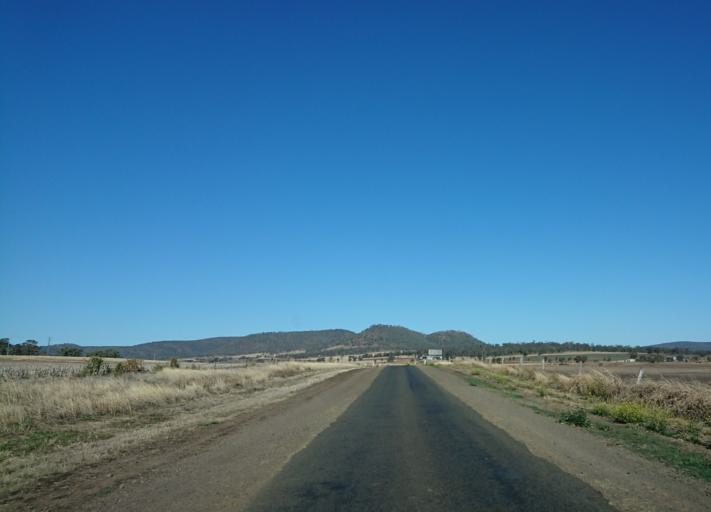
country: AU
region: Queensland
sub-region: Toowoomba
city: Top Camp
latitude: -27.8371
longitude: 152.0508
